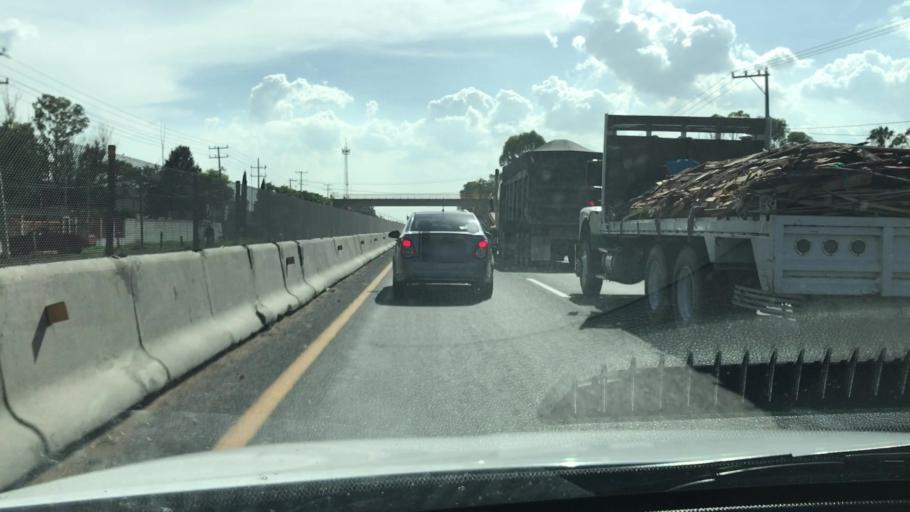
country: MX
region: Guanajuato
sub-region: Cortazar
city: Colonia la Calzada (La Olla)
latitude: 20.5102
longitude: -100.9670
